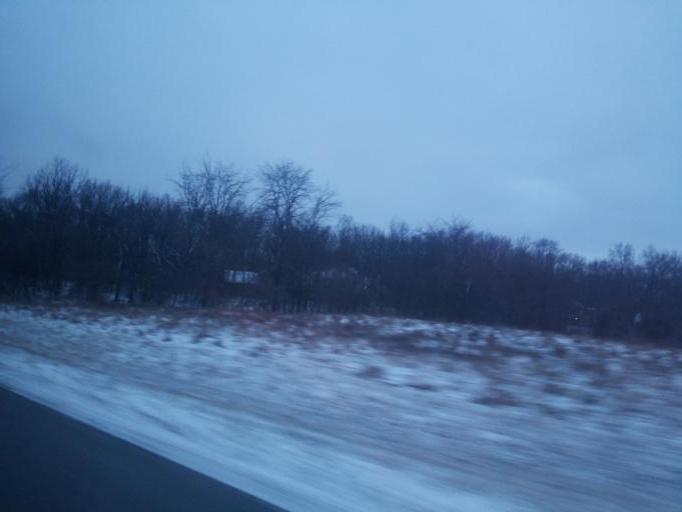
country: US
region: Ohio
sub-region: Delaware County
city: Sunbury
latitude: 40.2066
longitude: -82.8537
